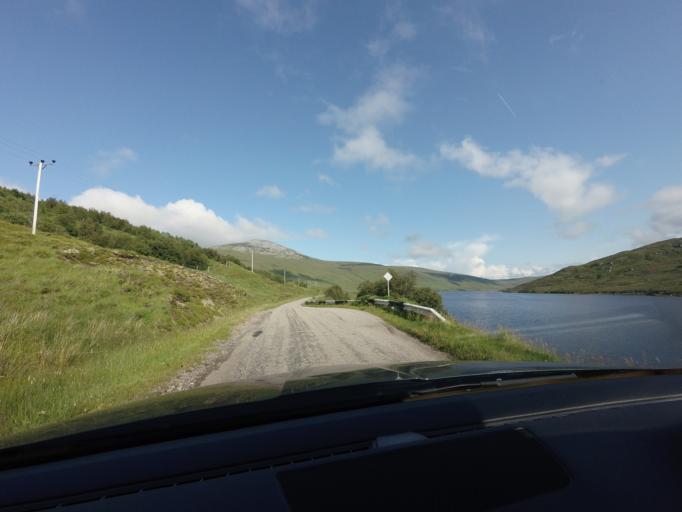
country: GB
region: Scotland
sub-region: Highland
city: Ullapool
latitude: 58.2568
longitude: -4.7718
